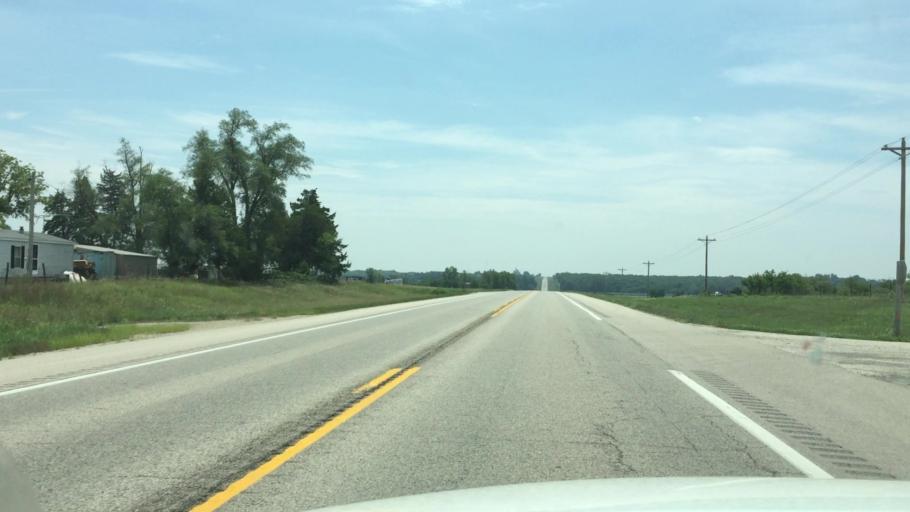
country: US
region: Kansas
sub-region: Jackson County
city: Holton
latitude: 39.6459
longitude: -95.7309
